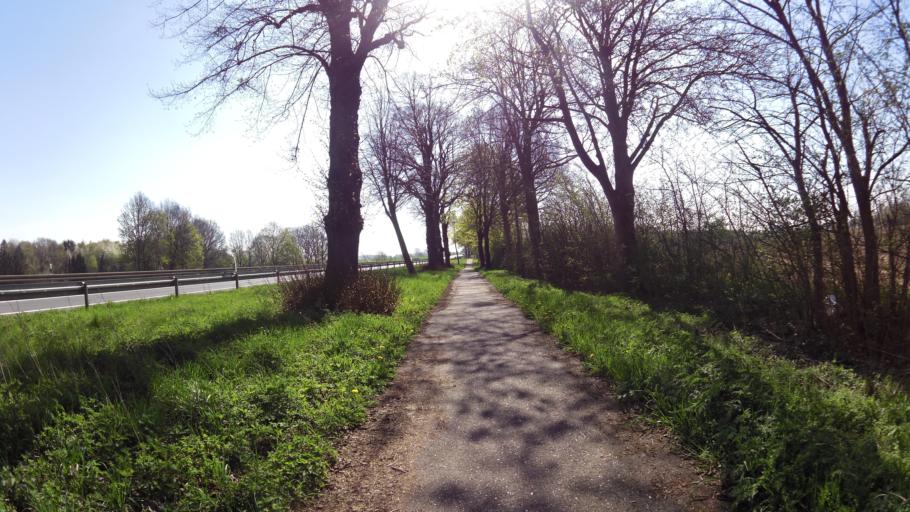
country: DE
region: North Rhine-Westphalia
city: Baesweiler
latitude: 50.9462
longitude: 6.1858
